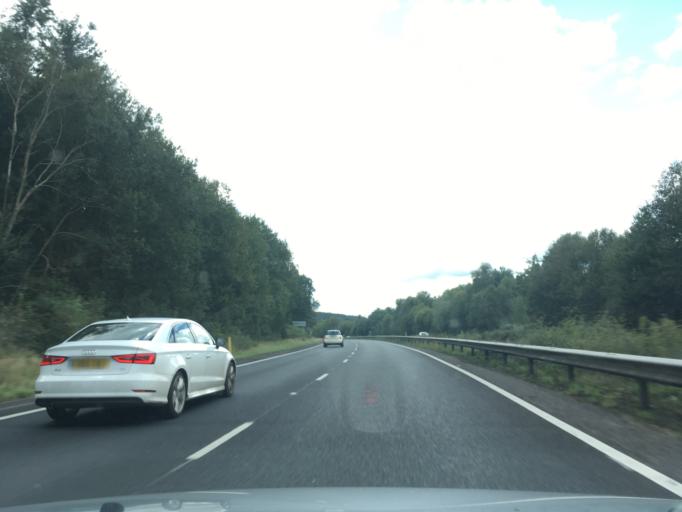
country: GB
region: England
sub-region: Hampshire
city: Liphook
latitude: 51.0831
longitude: -0.8287
